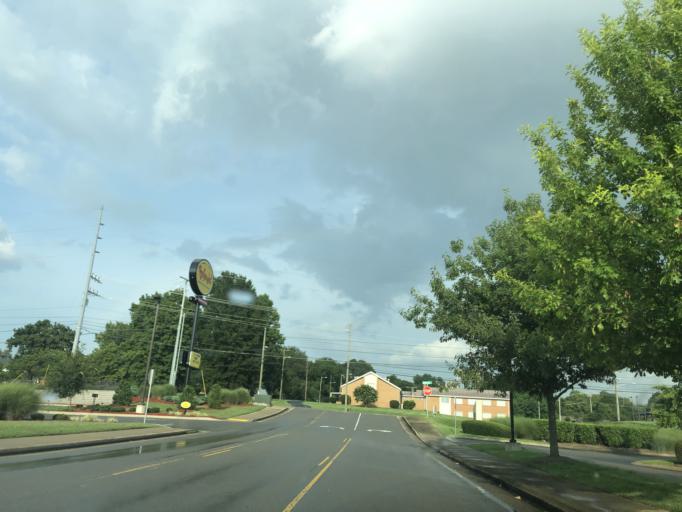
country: US
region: Tennessee
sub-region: Davidson County
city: Lakewood
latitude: 36.1539
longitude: -86.6664
